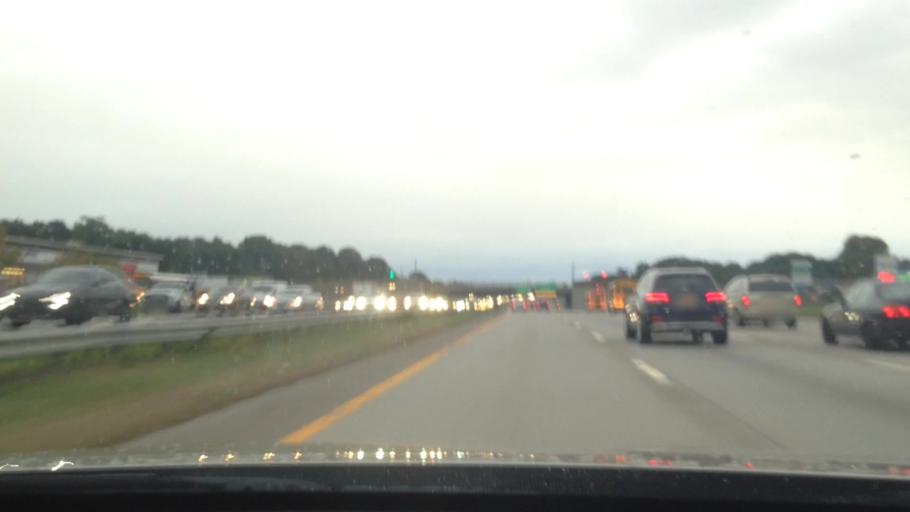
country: US
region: New York
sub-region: Suffolk County
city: Bohemia
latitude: 40.7559
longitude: -73.1105
